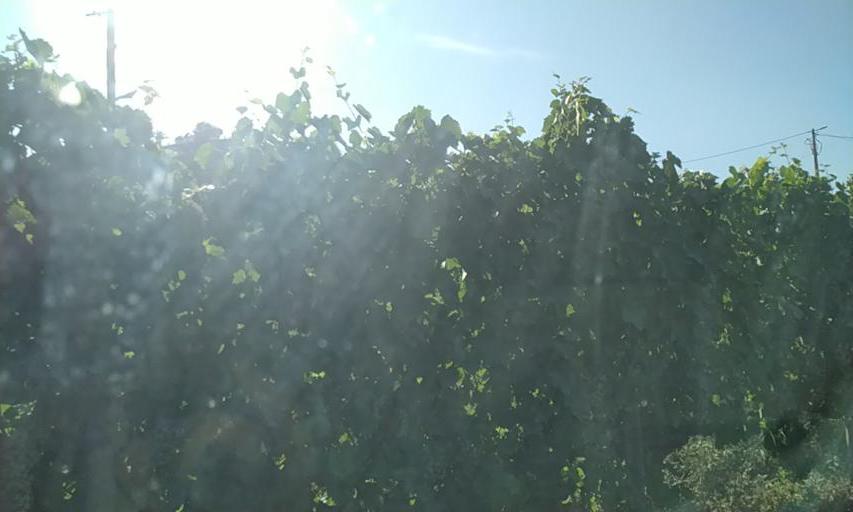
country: PT
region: Viseu
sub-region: Sao Joao da Pesqueira
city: Sao Joao da Pesqueira
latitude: 41.1863
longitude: -7.4097
